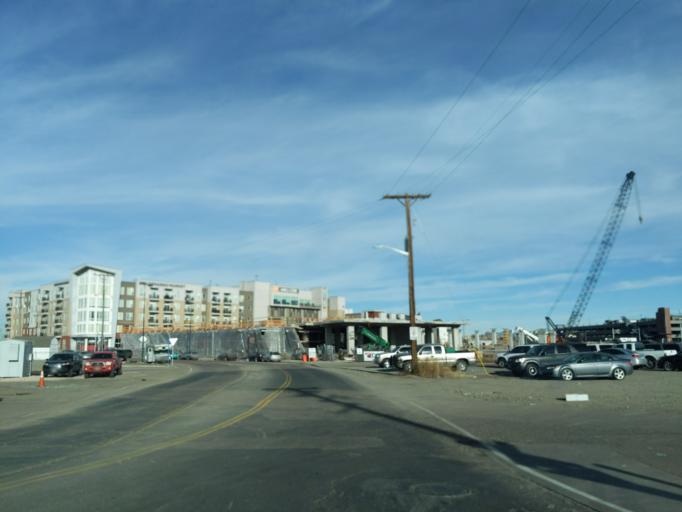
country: US
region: Colorado
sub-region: Denver County
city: Denver
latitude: 39.7606
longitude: -104.9917
